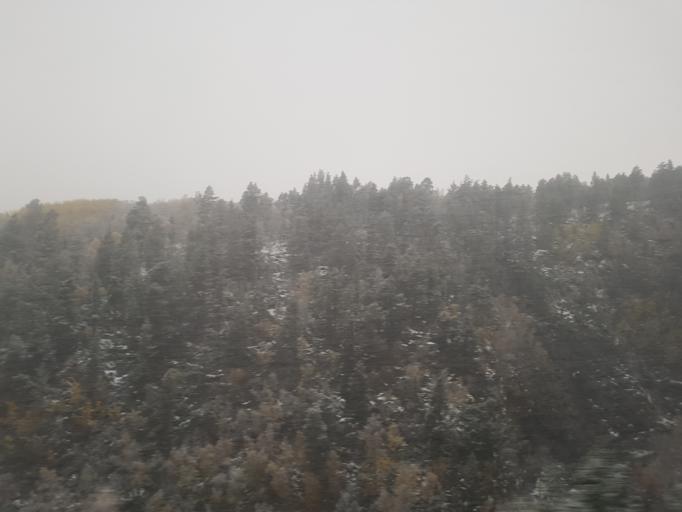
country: NO
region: Oppland
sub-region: Dovre
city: Dombas
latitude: 62.0780
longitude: 9.1296
